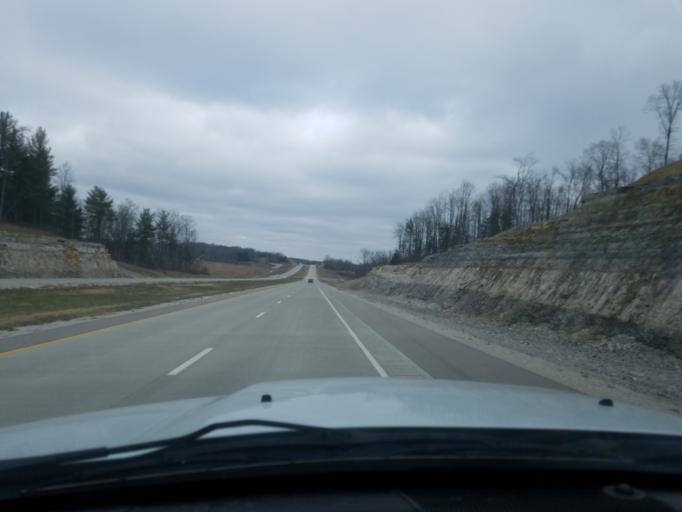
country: US
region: Indiana
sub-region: Monroe County
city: Bloomington
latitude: 39.0792
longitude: -86.5818
